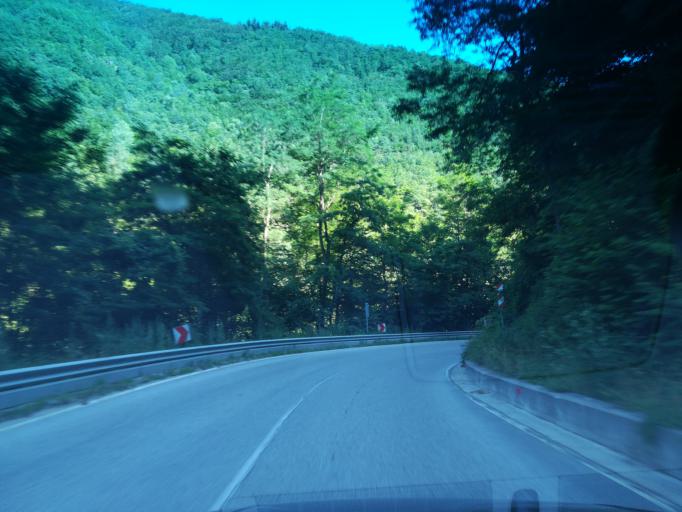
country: BG
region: Smolyan
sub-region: Obshtina Chepelare
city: Chepelare
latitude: 41.7942
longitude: 24.7109
